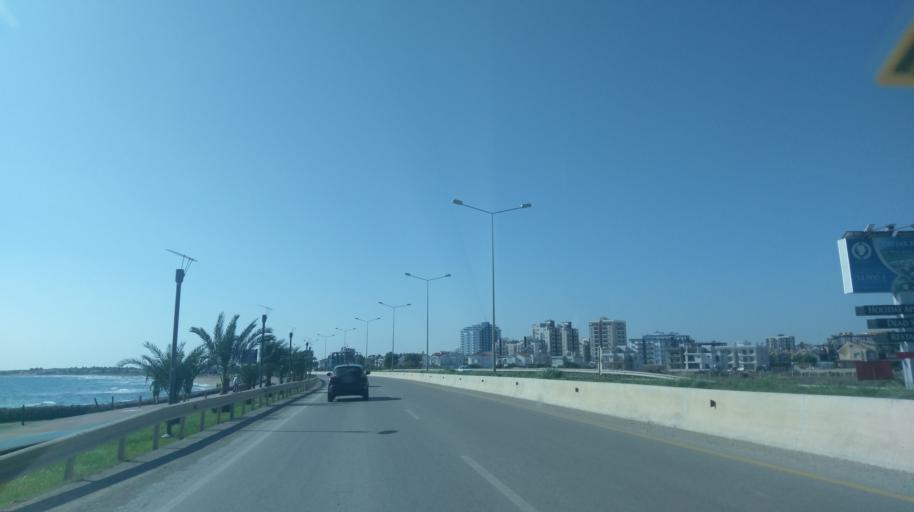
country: CY
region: Ammochostos
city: Trikomo
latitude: 35.2586
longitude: 33.9076
